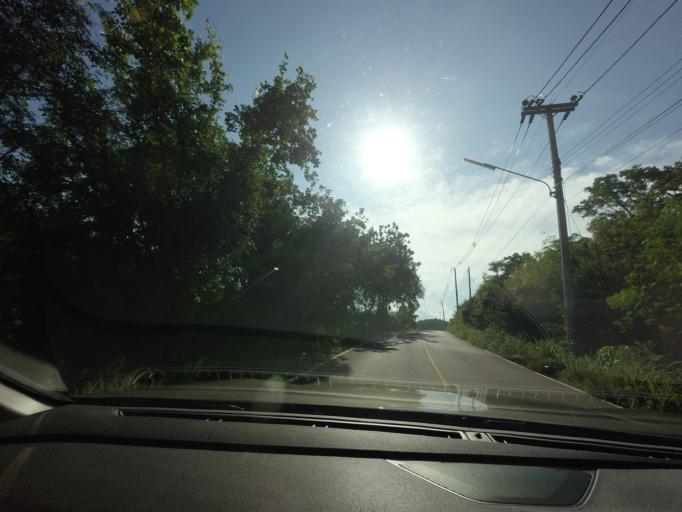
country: TH
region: Prachuap Khiri Khan
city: Pran Buri
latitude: 12.4116
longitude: 99.9719
